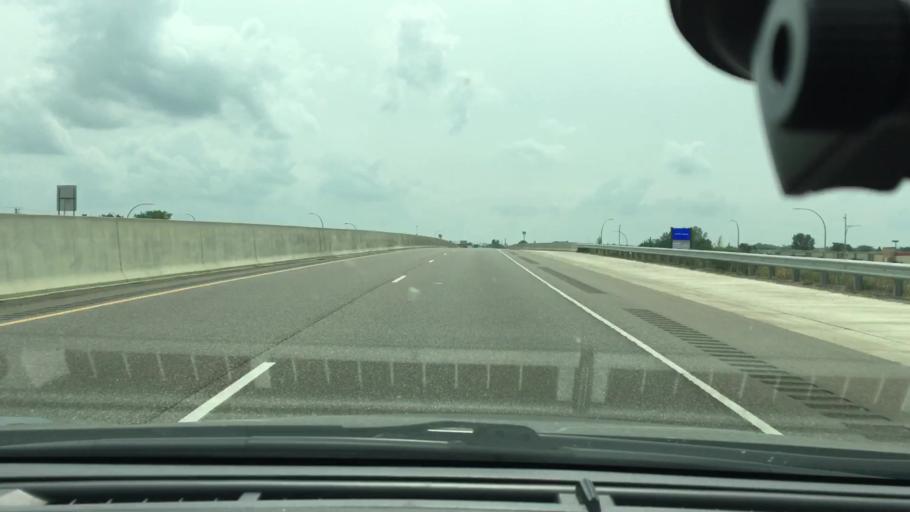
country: US
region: Minnesota
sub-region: Hennepin County
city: Rogers
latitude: 45.2118
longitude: -93.5526
